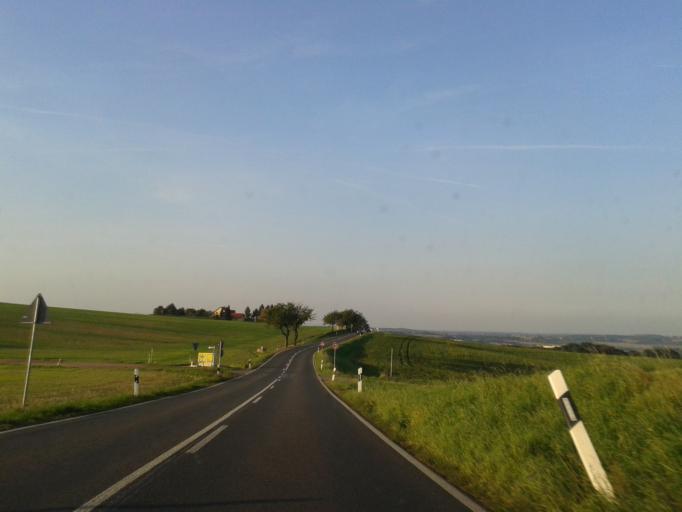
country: DE
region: Saxony
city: Meissen
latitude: 51.1396
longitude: 13.4736
